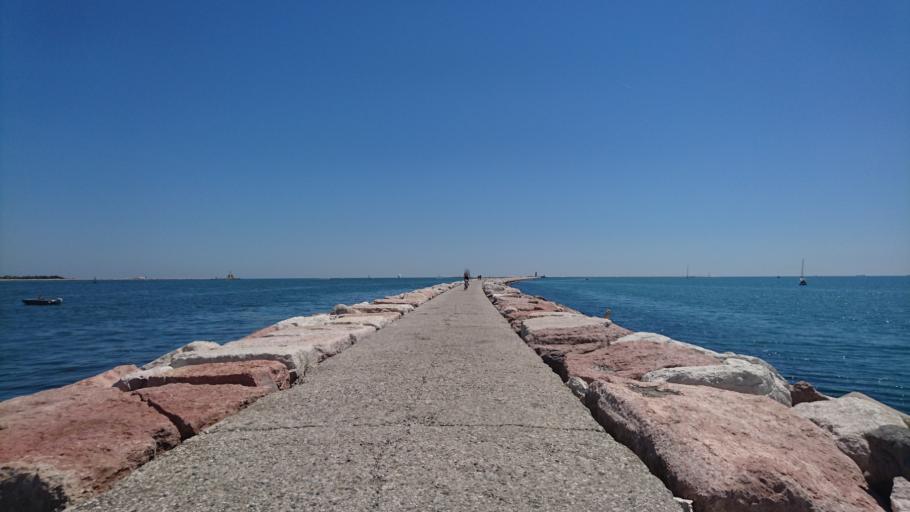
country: IT
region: Veneto
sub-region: Provincia di Venezia
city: Lido
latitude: 45.4264
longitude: 12.4139
